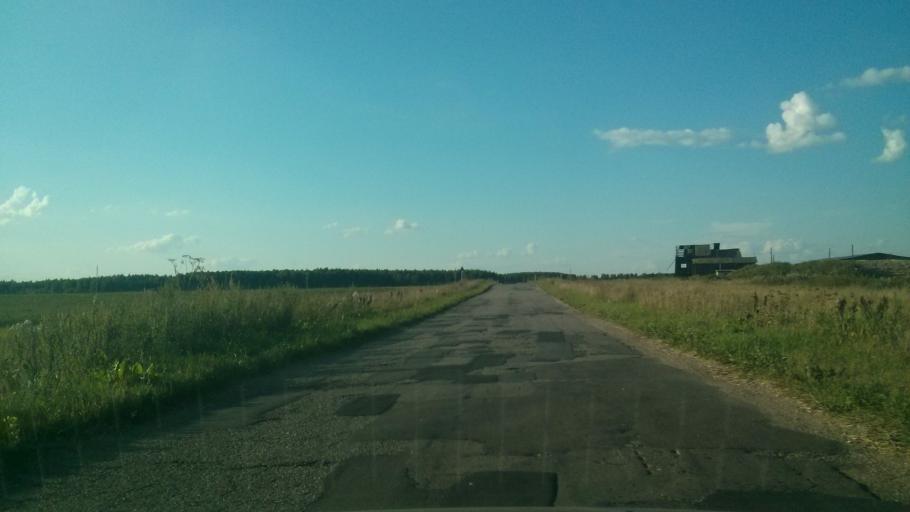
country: RU
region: Vladimir
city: Melenki
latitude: 55.3142
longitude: 41.7809
